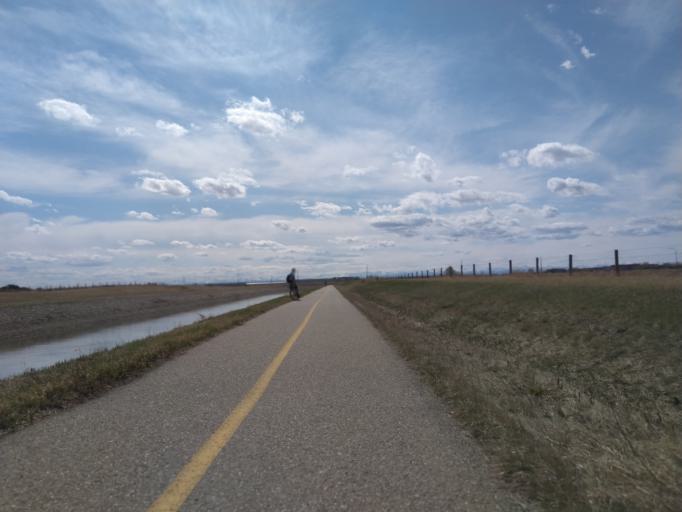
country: CA
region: Alberta
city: Chestermere
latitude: 50.9738
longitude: -113.9263
